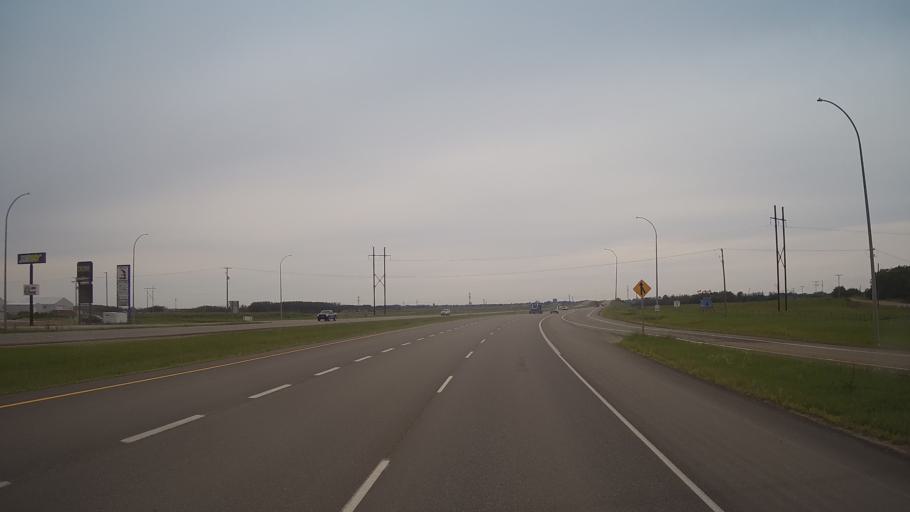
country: CA
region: Saskatchewan
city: Saskatoon
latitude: 52.0577
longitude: -106.5994
